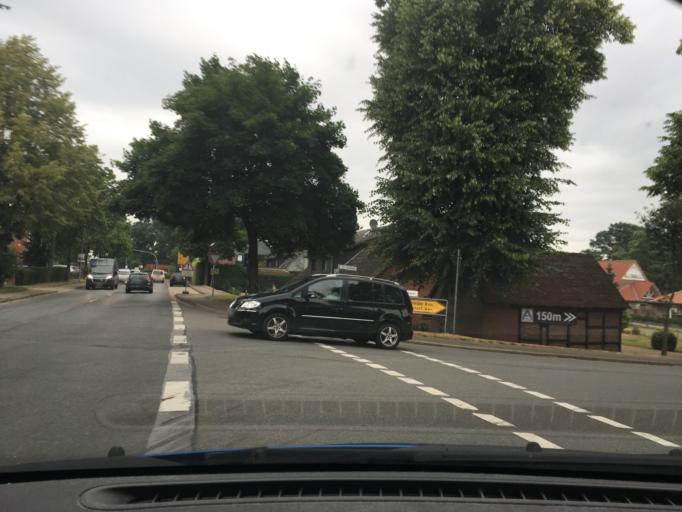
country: DE
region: Lower Saxony
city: Hollenstedt
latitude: 53.3655
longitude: 9.7116
